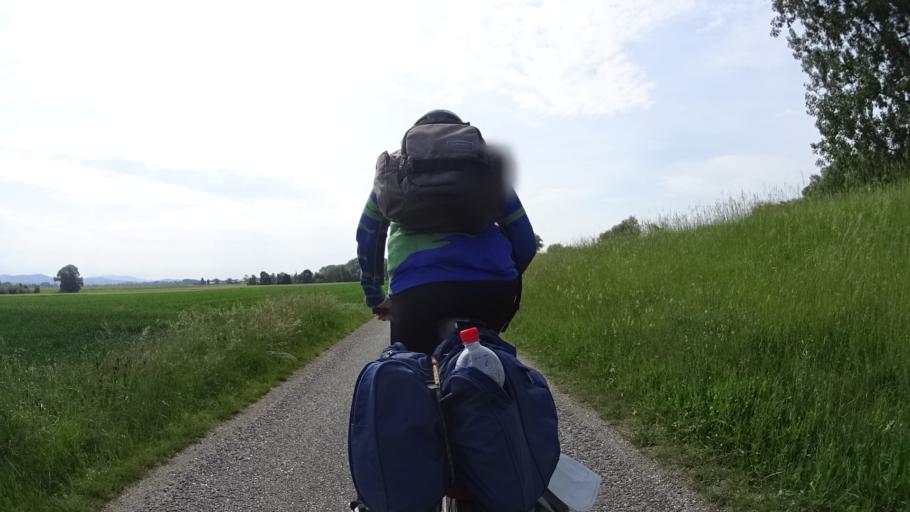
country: DE
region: Bavaria
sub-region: Lower Bavaria
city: Mariaposching
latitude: 48.8320
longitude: 12.7849
